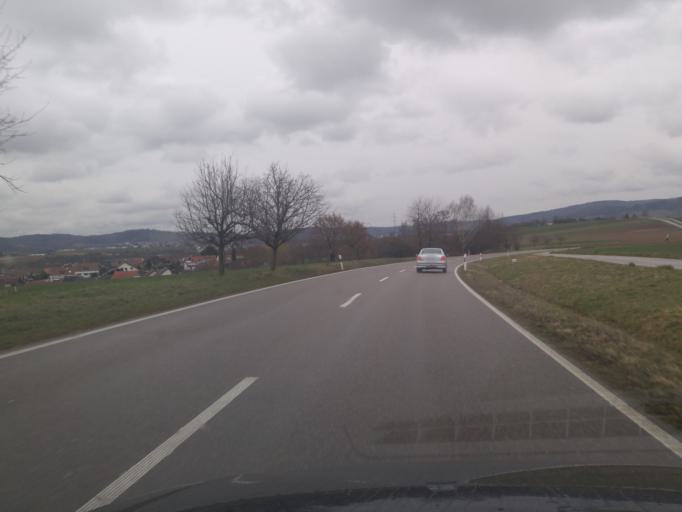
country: DE
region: Baden-Wuerttemberg
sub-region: Regierungsbezirk Stuttgart
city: Schwaikheim
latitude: 48.8976
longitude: 9.3595
